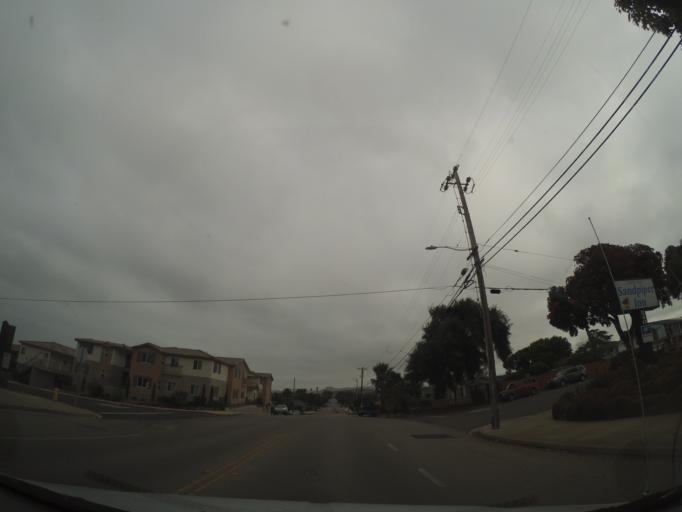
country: US
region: California
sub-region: San Luis Obispo County
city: Morro Bay
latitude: 35.3629
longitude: -120.8500
